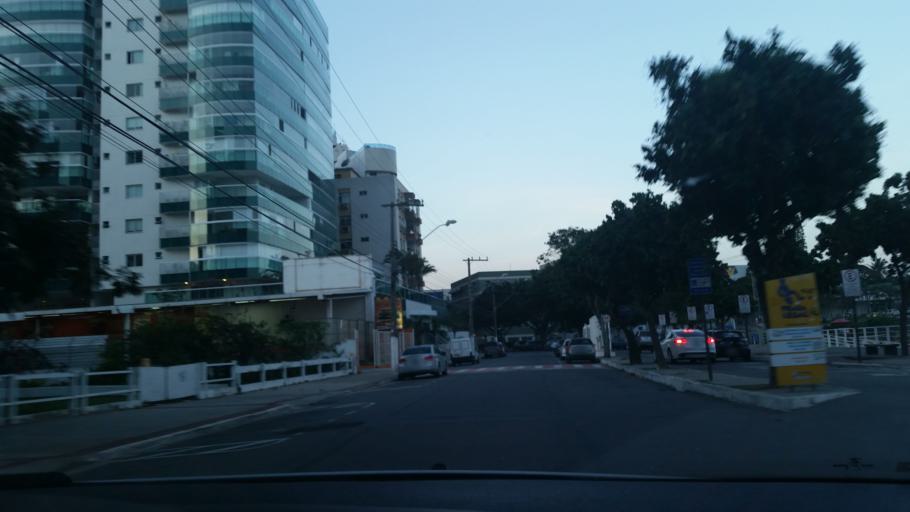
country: BR
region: Espirito Santo
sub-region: Vila Velha
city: Vila Velha
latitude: -20.3301
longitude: -40.2738
